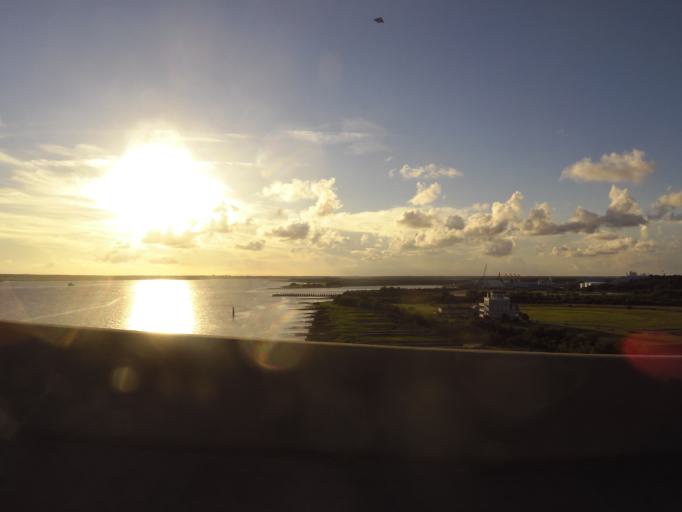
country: US
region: Georgia
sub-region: Glynn County
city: Brunswick
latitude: 31.1227
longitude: -81.4821
